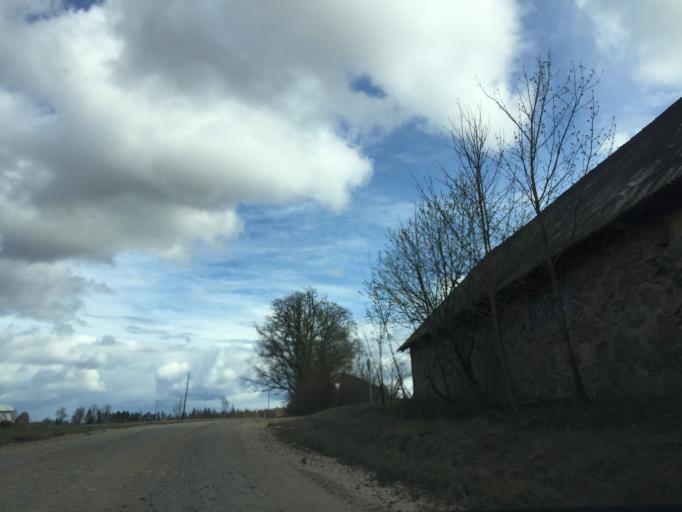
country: LV
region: Limbazu Rajons
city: Limbazi
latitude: 57.6077
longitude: 24.7930
